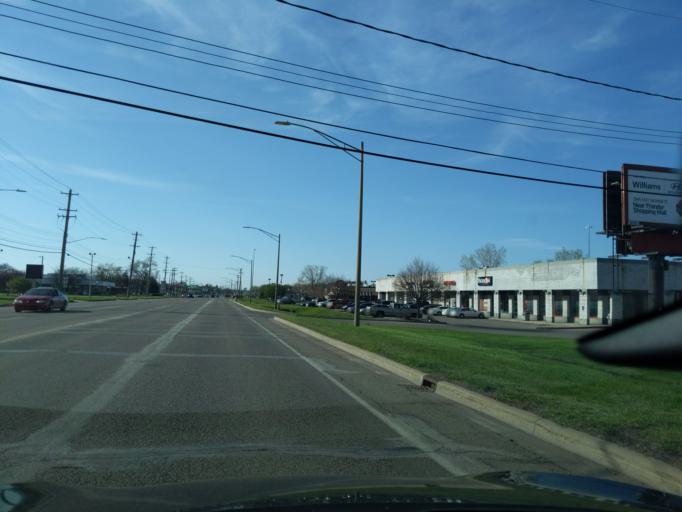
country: US
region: Michigan
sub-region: Ingham County
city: Holt
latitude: 42.6628
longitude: -84.5395
